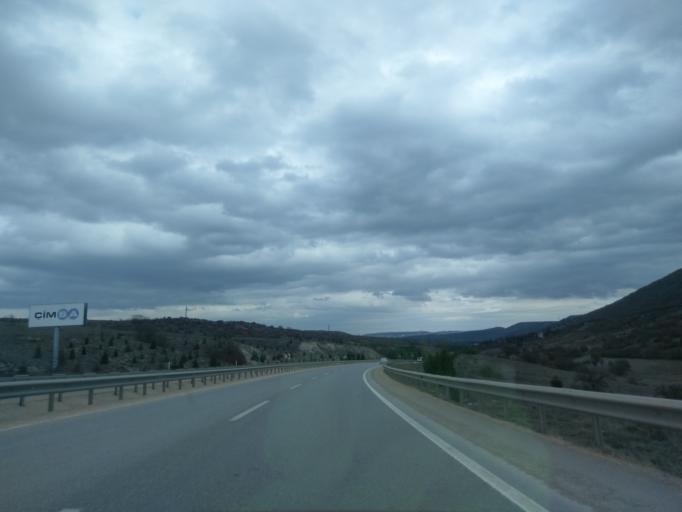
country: TR
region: Eskisehir
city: Eskisehir
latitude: 39.7421
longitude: 30.3969
